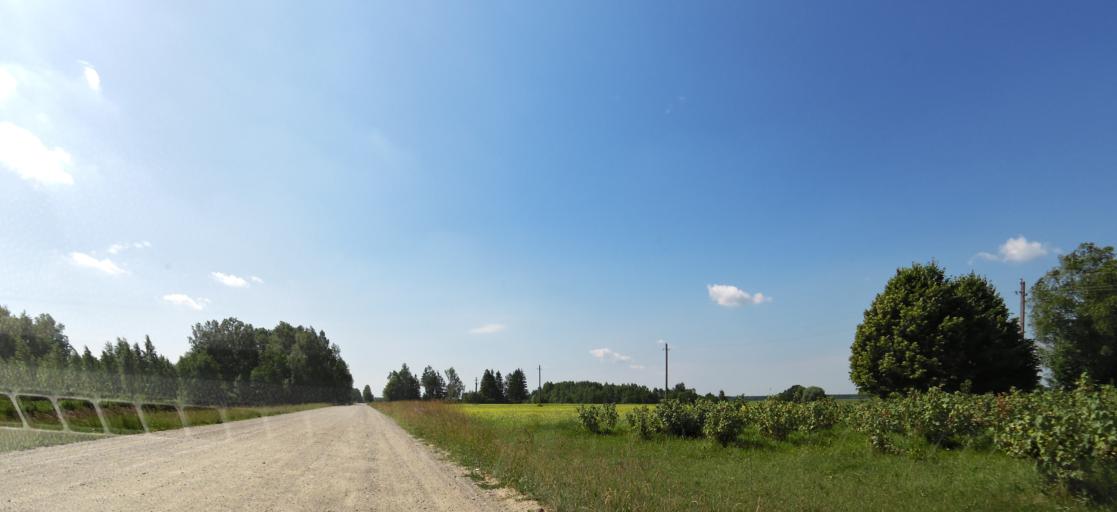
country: LT
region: Panevezys
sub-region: Birzai
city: Birzai
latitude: 56.1855
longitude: 24.9368
